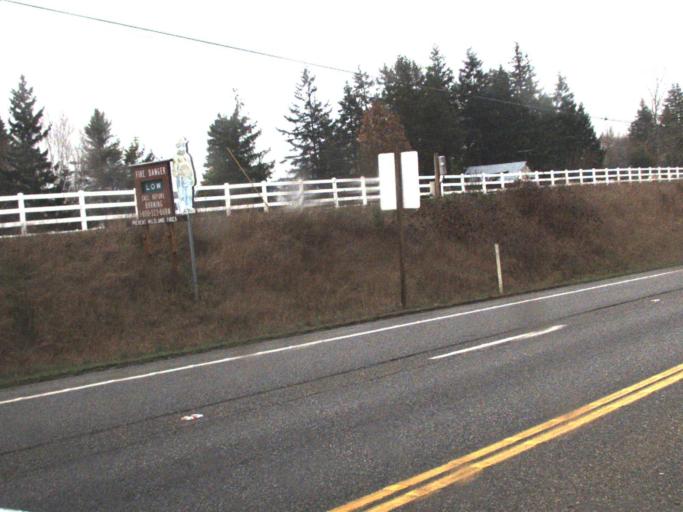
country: US
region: Washington
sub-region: Snohomish County
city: Stanwood
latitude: 48.2398
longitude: -122.4052
